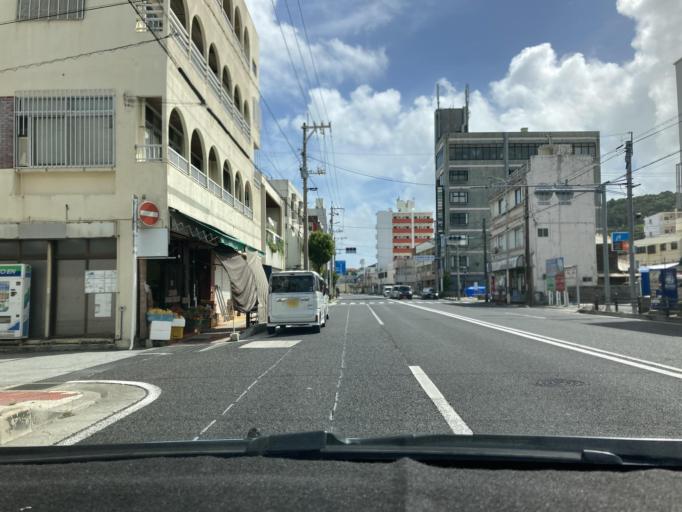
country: JP
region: Okinawa
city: Ginowan
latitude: 26.2008
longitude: 127.7570
